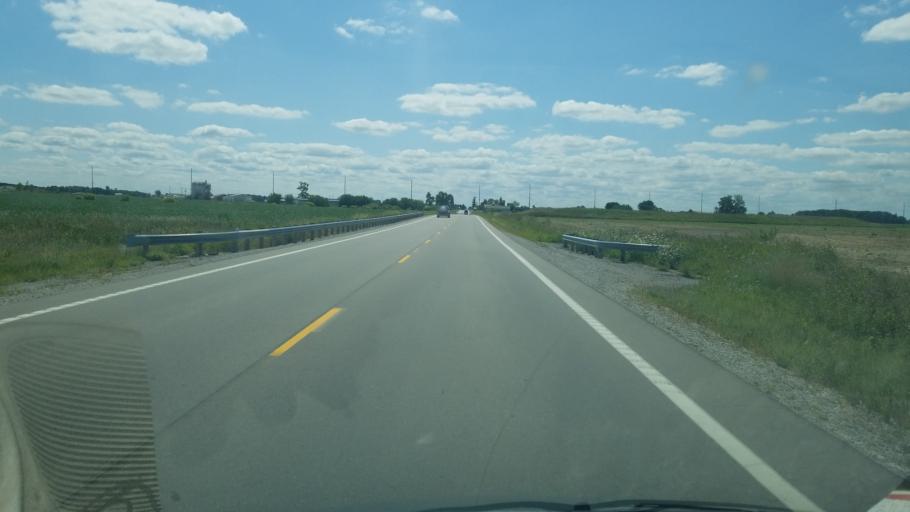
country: US
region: Ohio
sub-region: Fulton County
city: Delta
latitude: 41.7061
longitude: -84.0370
